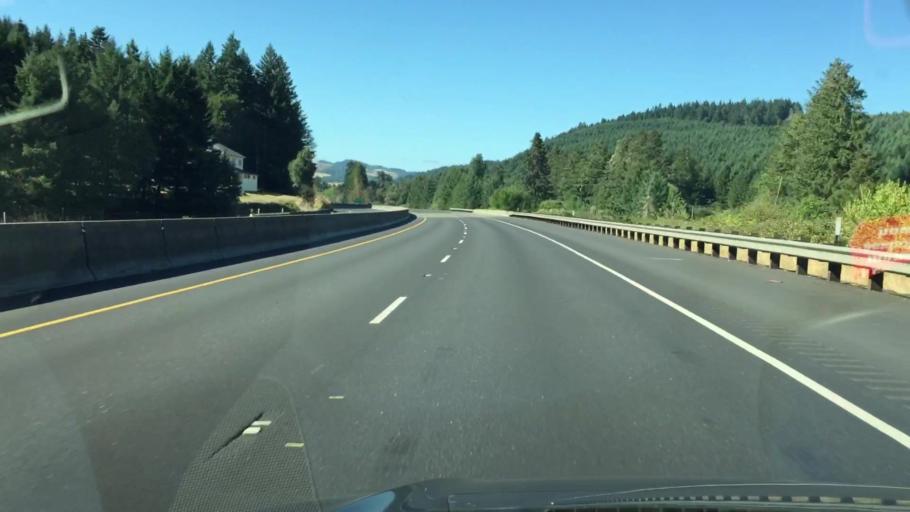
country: US
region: Oregon
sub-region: Lane County
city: Cottage Grove
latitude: 43.7386
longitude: -123.1890
